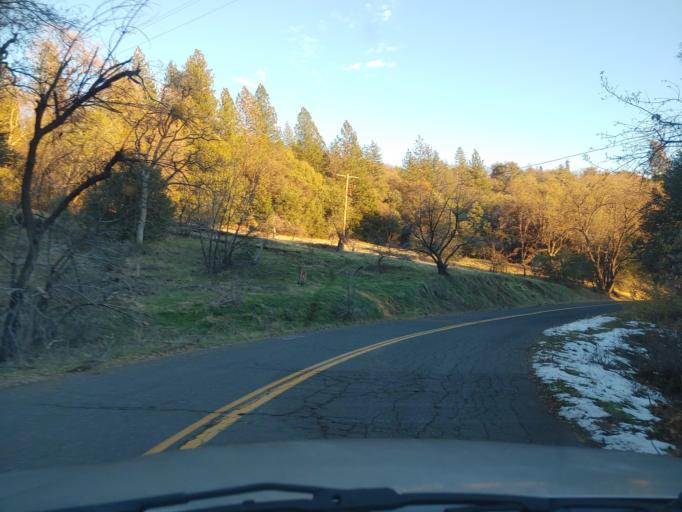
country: US
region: California
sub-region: Tuolumne County
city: Cedar Ridge
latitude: 38.0417
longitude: -120.3134
